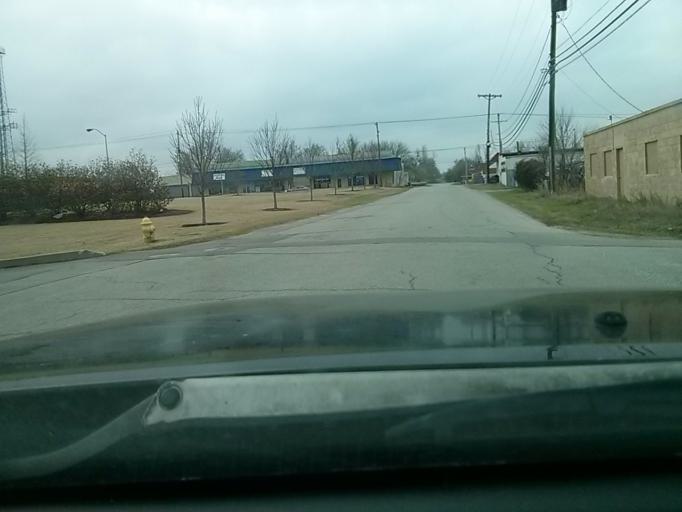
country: US
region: Oklahoma
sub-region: Tulsa County
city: Tulsa
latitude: 36.1618
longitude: -95.9180
